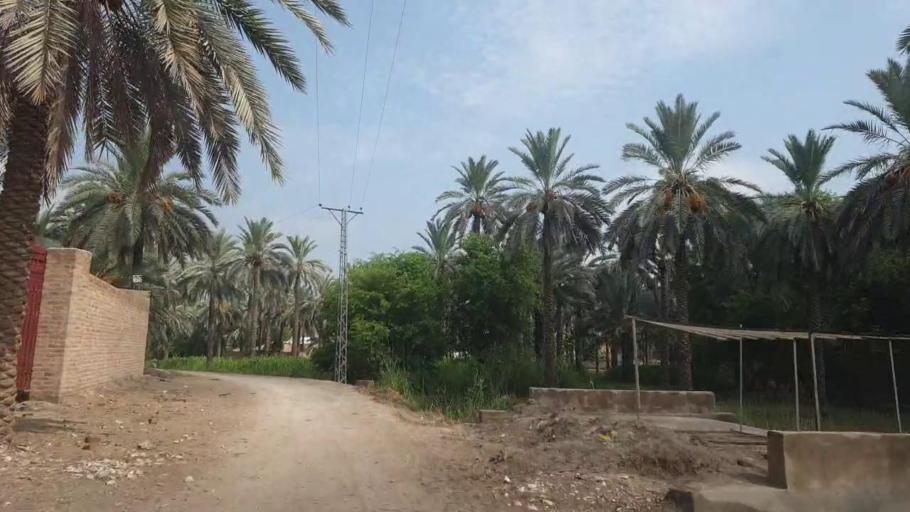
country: PK
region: Sindh
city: Khairpur
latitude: 27.5609
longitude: 68.7640
